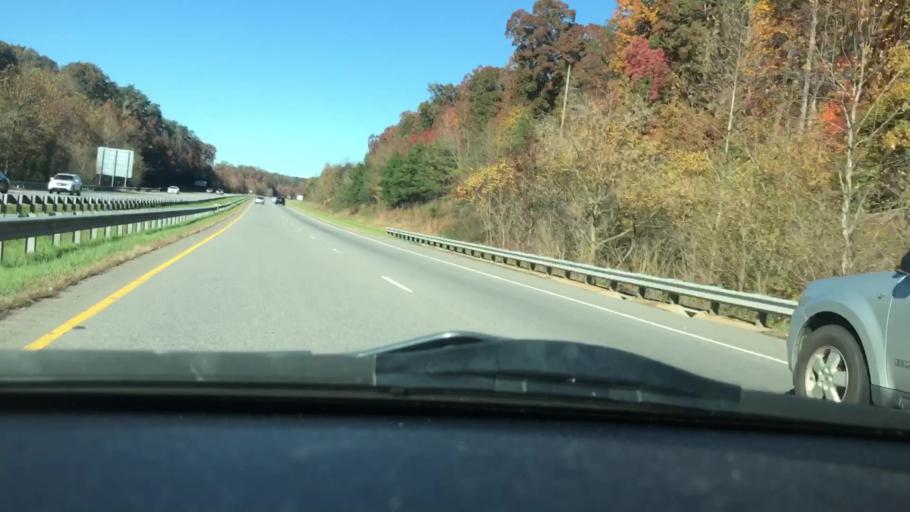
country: US
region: North Carolina
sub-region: Rockingham County
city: Madison
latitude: 36.3864
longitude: -79.9411
